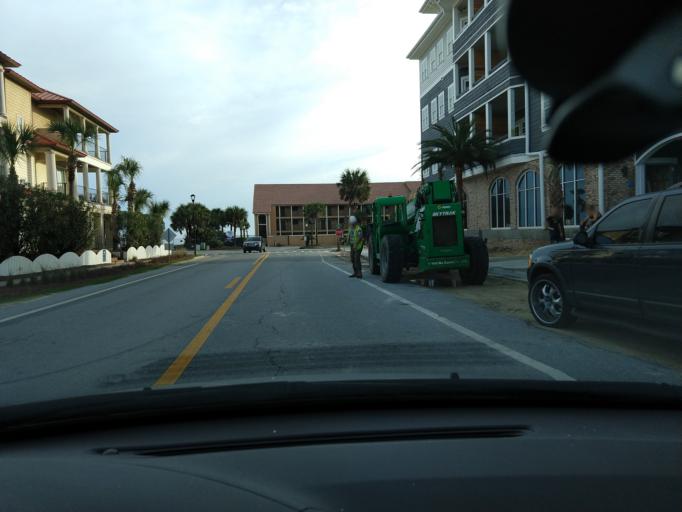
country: US
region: Florida
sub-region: Okaloosa County
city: Destin
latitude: 30.3836
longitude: -86.4306
